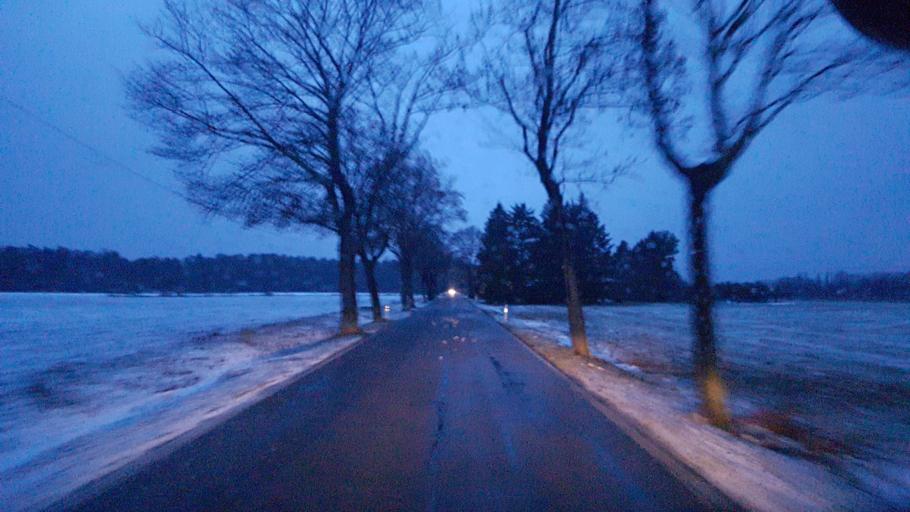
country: DE
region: Brandenburg
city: Guhrow
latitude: 51.7954
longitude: 14.2186
